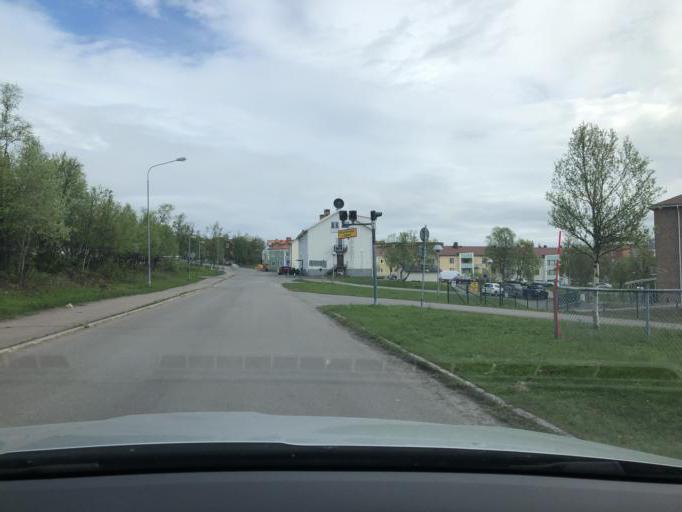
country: SE
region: Norrbotten
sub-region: Kiruna Kommun
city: Kiruna
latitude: 67.8503
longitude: 20.2355
